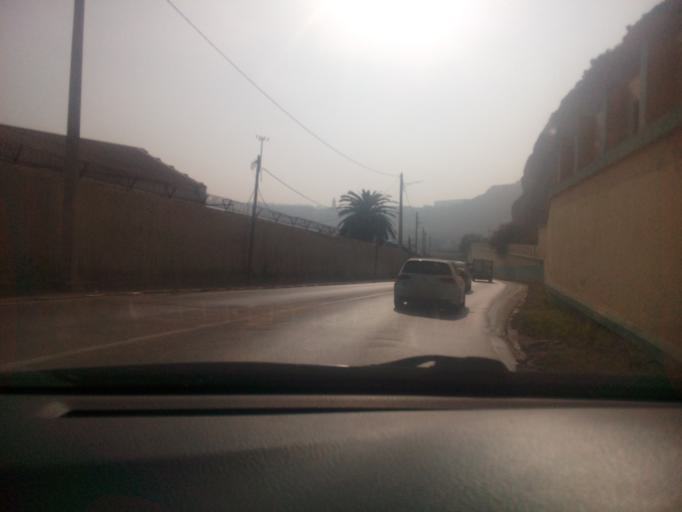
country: DZ
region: Oran
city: Oran
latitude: 35.7132
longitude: -0.6569
